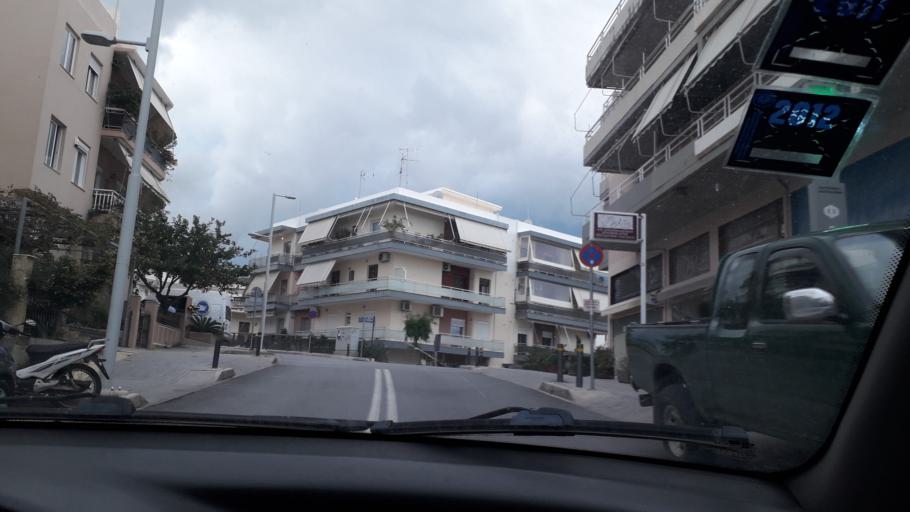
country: GR
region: Crete
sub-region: Nomos Rethymnis
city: Rethymno
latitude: 35.3635
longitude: 24.4727
